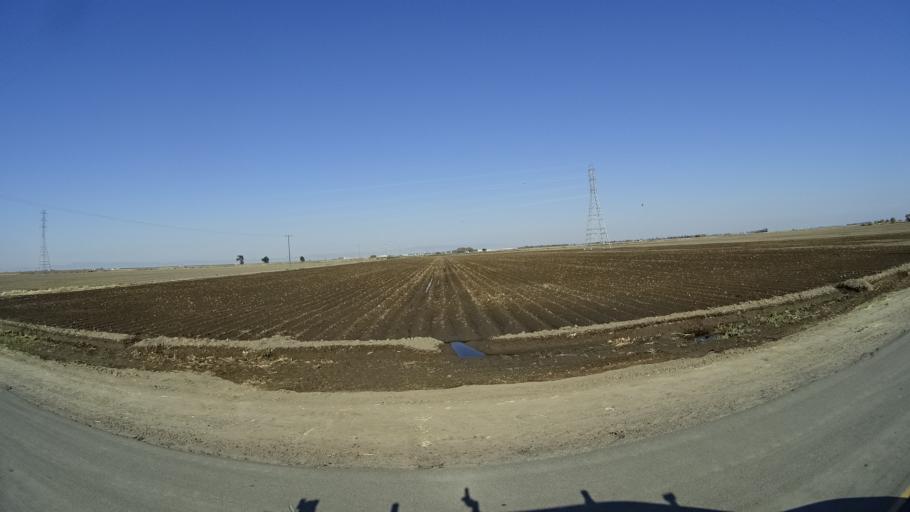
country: US
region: California
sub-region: Kings County
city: Lemoore Station
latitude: 36.3288
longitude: -119.8873
